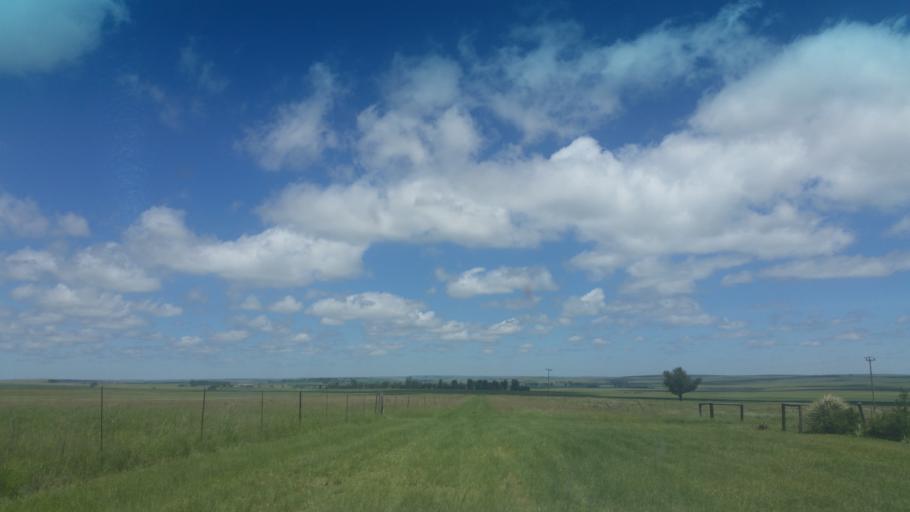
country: ZA
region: Orange Free State
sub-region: Thabo Mofutsanyana District Municipality
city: Harrismith
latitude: -28.1932
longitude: 29.0130
